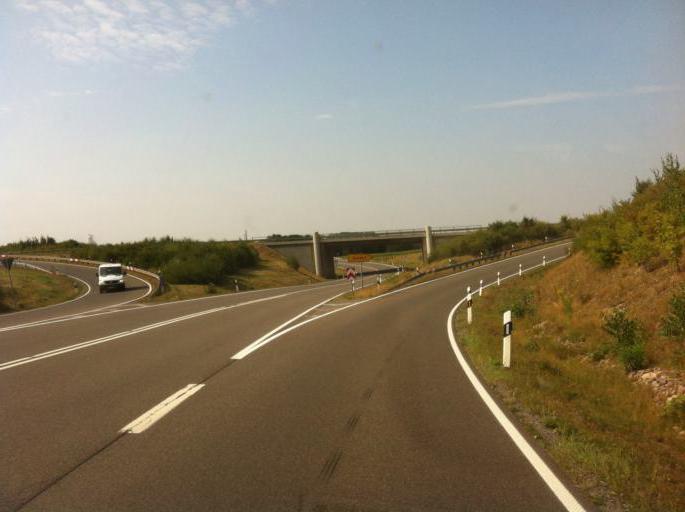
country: DE
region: Saxony
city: Neumark
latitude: 50.6372
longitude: 12.3477
